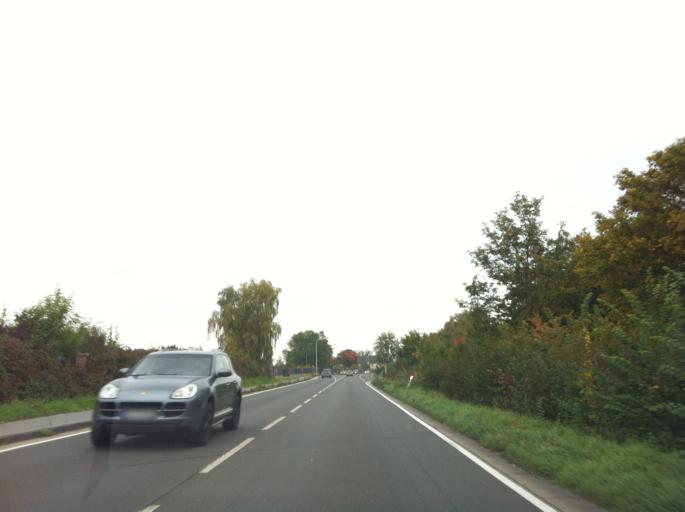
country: DE
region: North Rhine-Westphalia
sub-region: Regierungsbezirk Koln
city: Dueren
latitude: 50.7835
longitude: 6.5076
